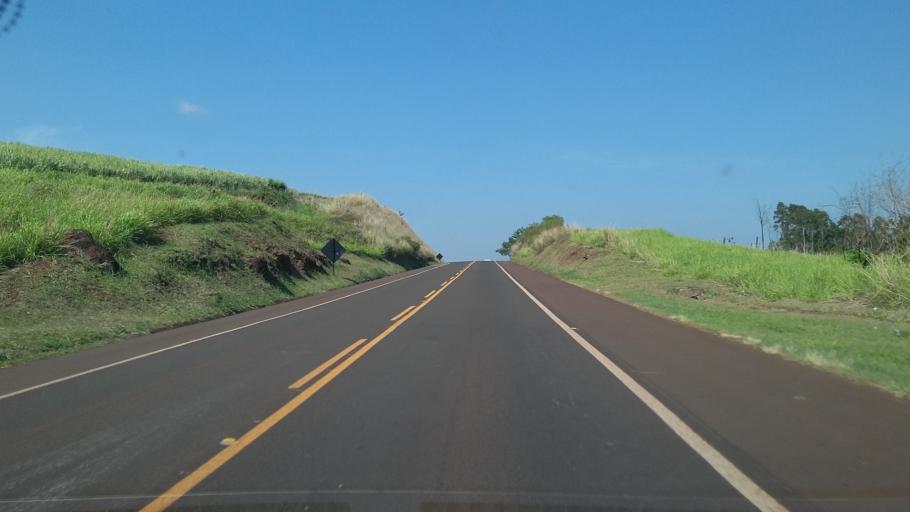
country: BR
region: Parana
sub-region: Bandeirantes
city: Bandeirantes
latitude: -23.1287
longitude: -50.3651
